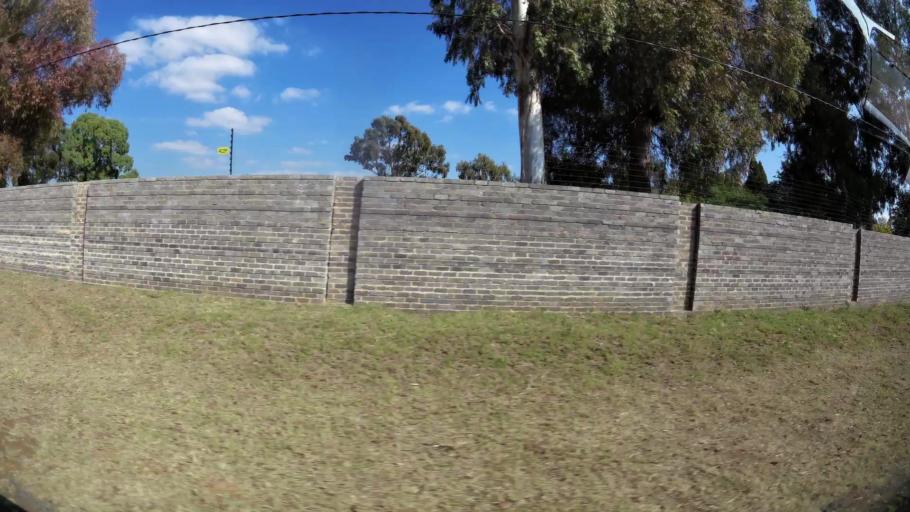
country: ZA
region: Gauteng
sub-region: Ekurhuleni Metropolitan Municipality
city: Benoni
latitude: -26.0855
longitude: 28.3560
